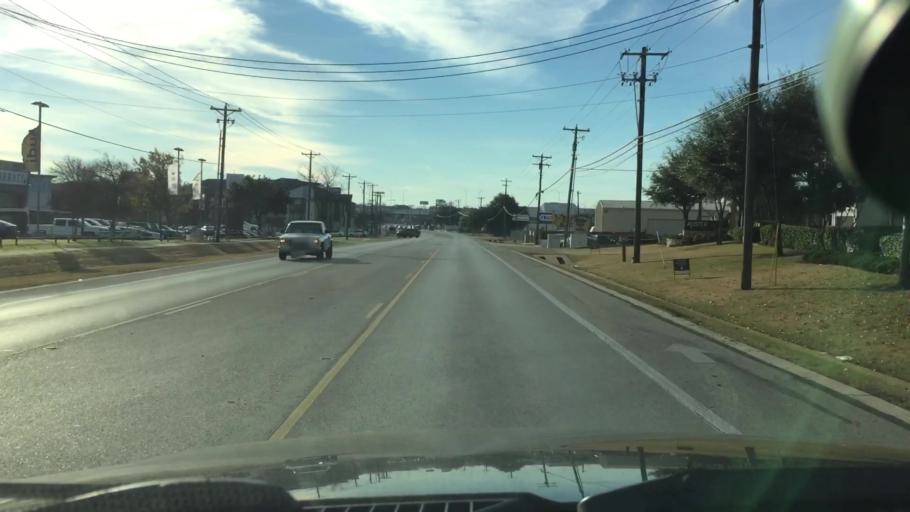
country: US
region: Texas
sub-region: Williamson County
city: Jollyville
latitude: 30.4399
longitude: -97.7728
